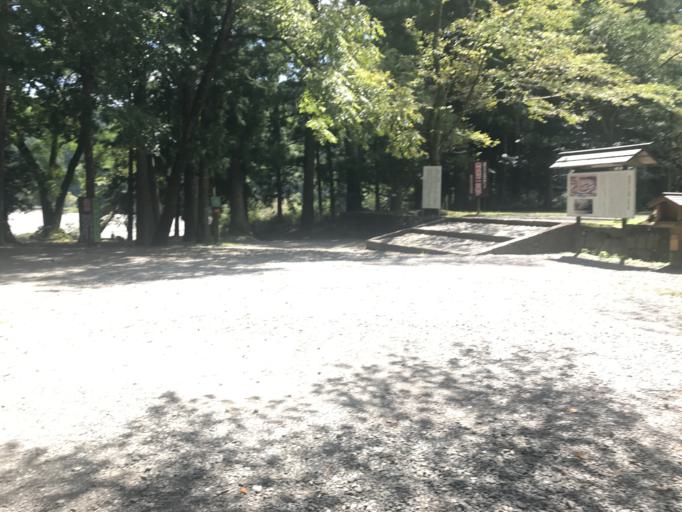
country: JP
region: Wakayama
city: Shingu
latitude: 33.8347
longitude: 135.7751
